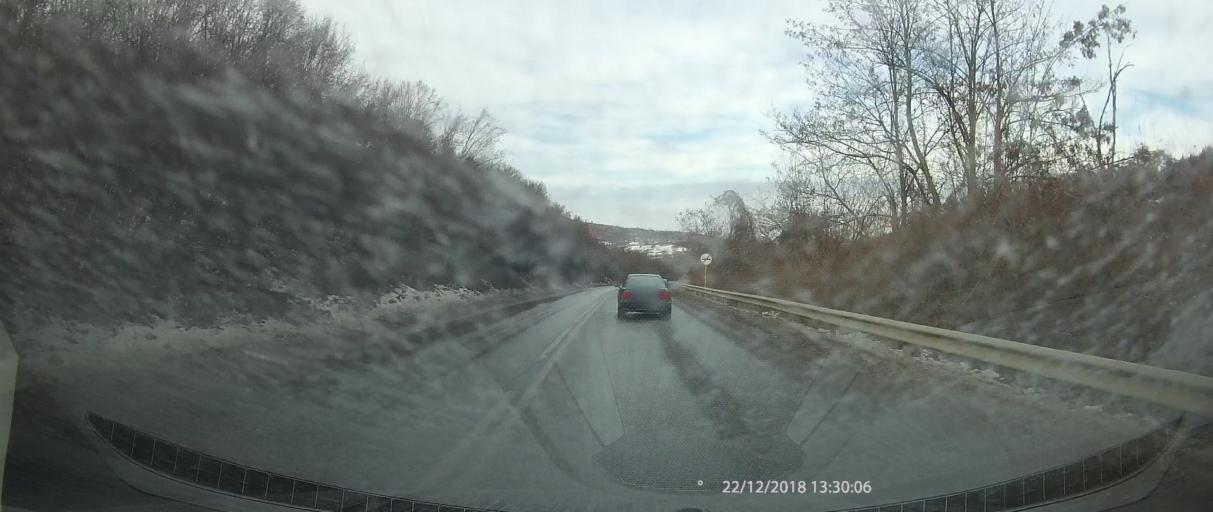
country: BG
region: Lovech
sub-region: Obshtina Yablanitsa
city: Yablanitsa
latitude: 43.0849
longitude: 24.1489
